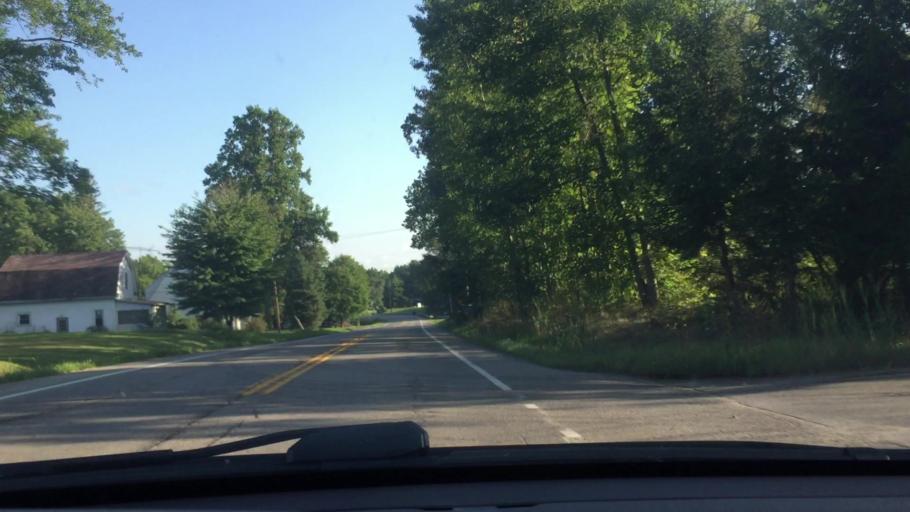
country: US
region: Pennsylvania
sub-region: Mercer County
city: Grove City
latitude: 41.1749
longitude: -80.0837
